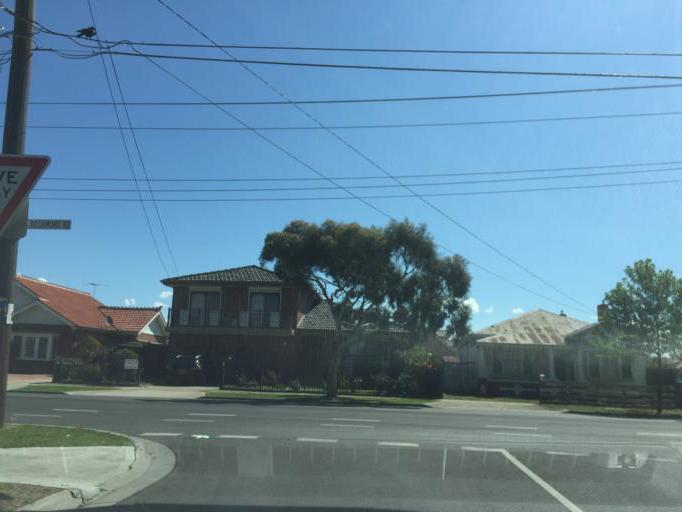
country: AU
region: Victoria
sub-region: Maribyrnong
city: Maribyrnong
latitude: -37.7812
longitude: 144.8847
